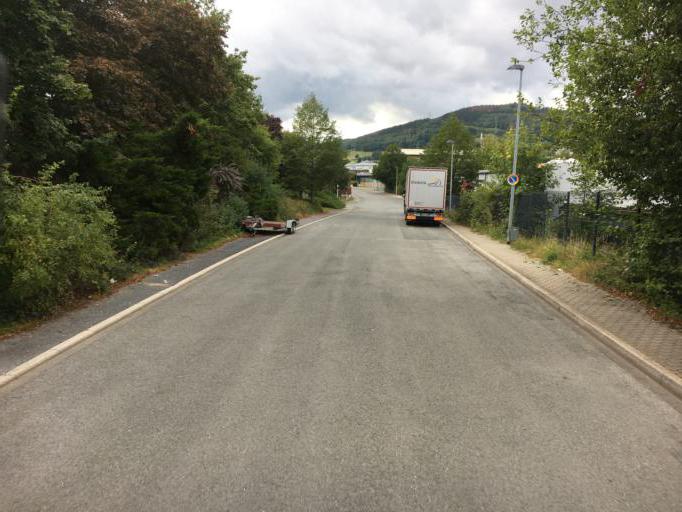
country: DE
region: North Rhine-Westphalia
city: Plettenberg
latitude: 51.1965
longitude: 7.8390
